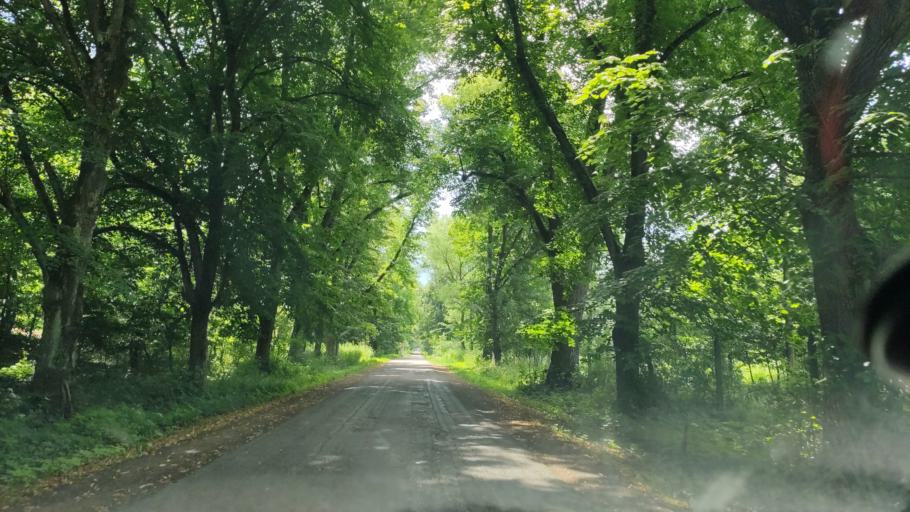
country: HU
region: Heves
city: Parad
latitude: 47.9114
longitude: 20.0574
